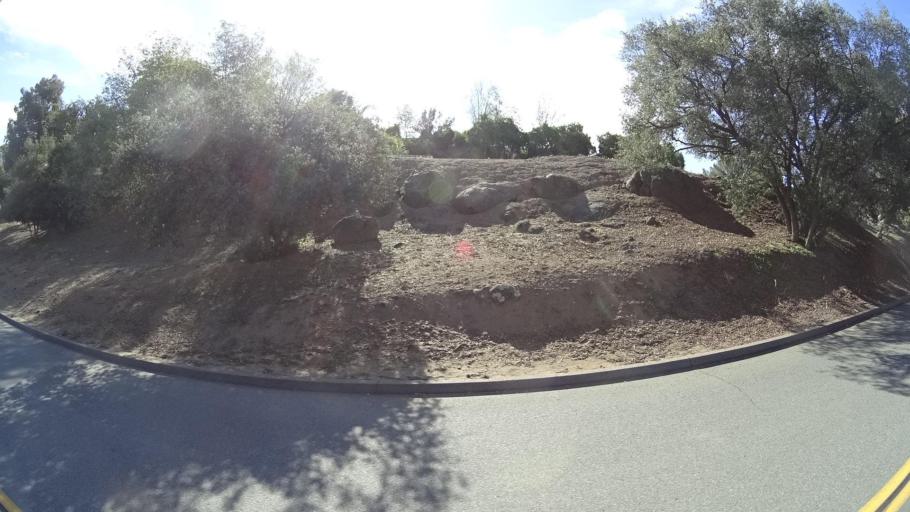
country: US
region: California
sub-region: San Diego County
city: Alpine
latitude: 32.8219
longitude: -116.7475
